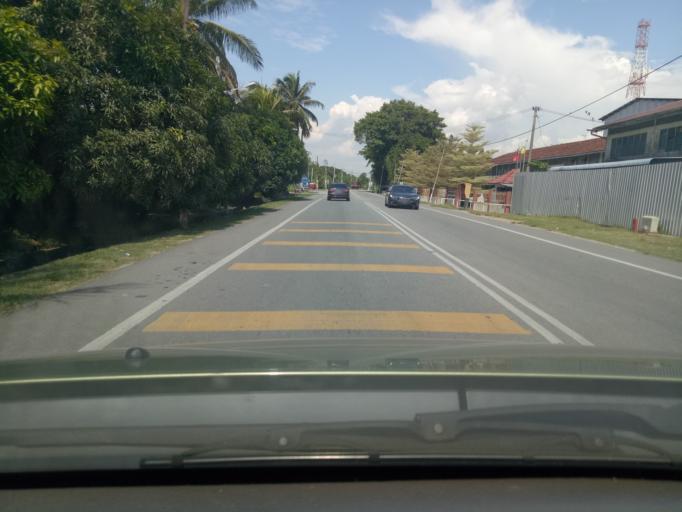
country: MY
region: Kedah
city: Alor Setar
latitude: 5.9739
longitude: 100.4020
